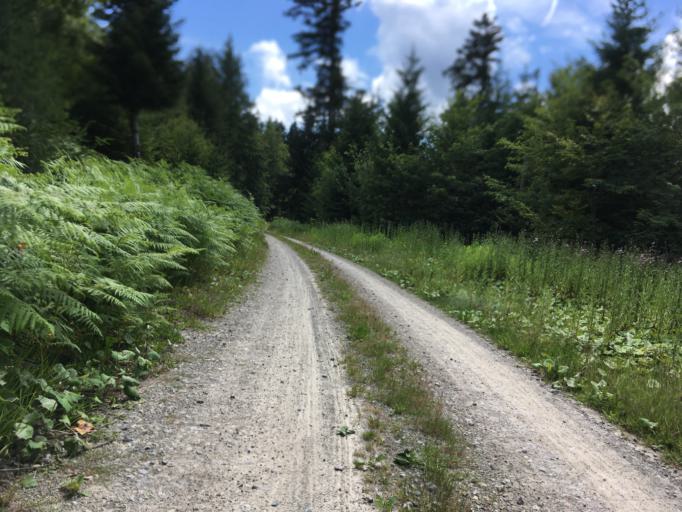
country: DE
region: Baden-Wuerttemberg
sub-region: Karlsruhe Region
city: Baiersbronn
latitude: 48.5675
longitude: 8.4177
